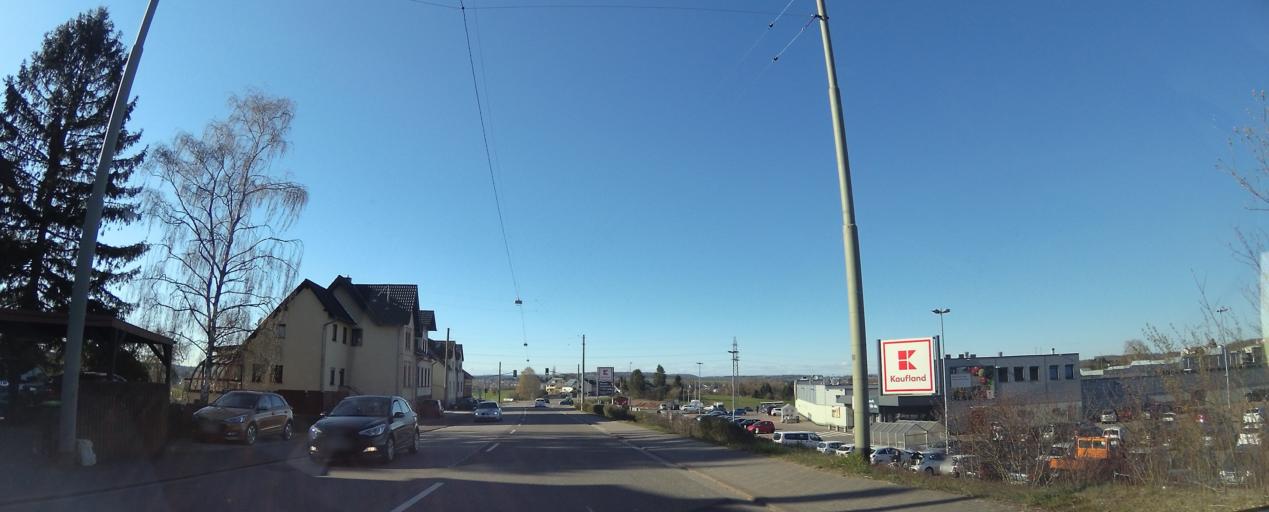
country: DE
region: Saarland
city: Riegelsberg
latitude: 49.3218
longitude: 6.9387
